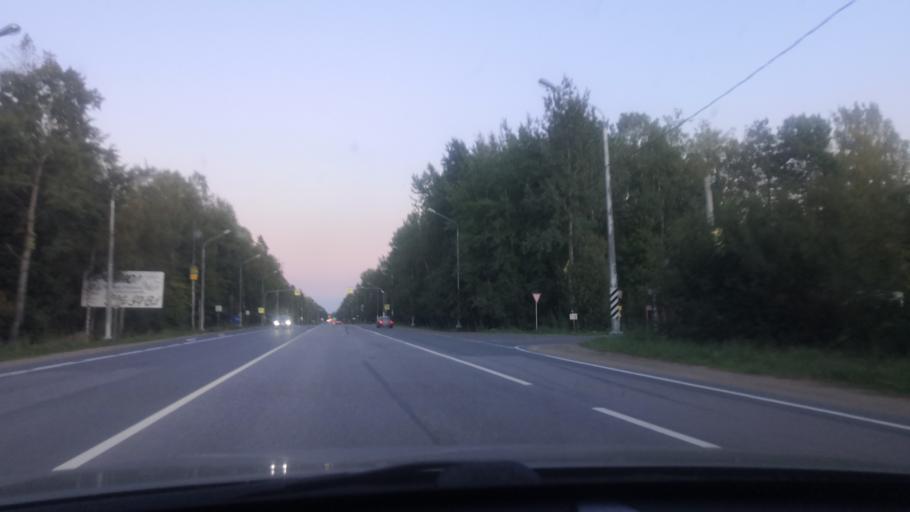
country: RU
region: St.-Petersburg
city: Pesochnyy
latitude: 60.1896
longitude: 30.0962
